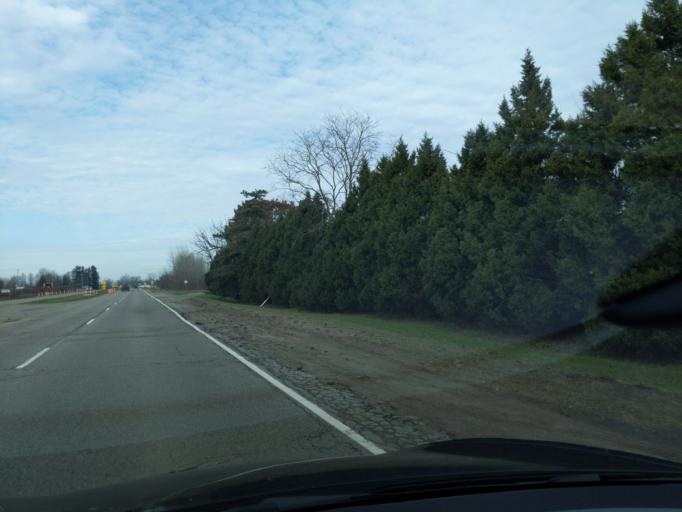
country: US
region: Michigan
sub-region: Ingham County
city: Holt
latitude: 42.6289
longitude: -84.5044
